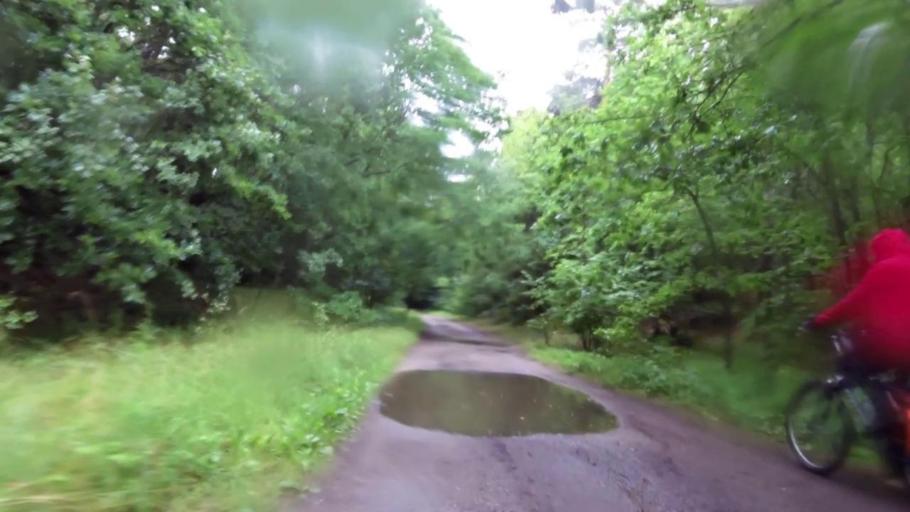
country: PL
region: West Pomeranian Voivodeship
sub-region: Powiat kolobrzeski
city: Ustronie Morskie
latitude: 54.2354
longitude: 15.8319
